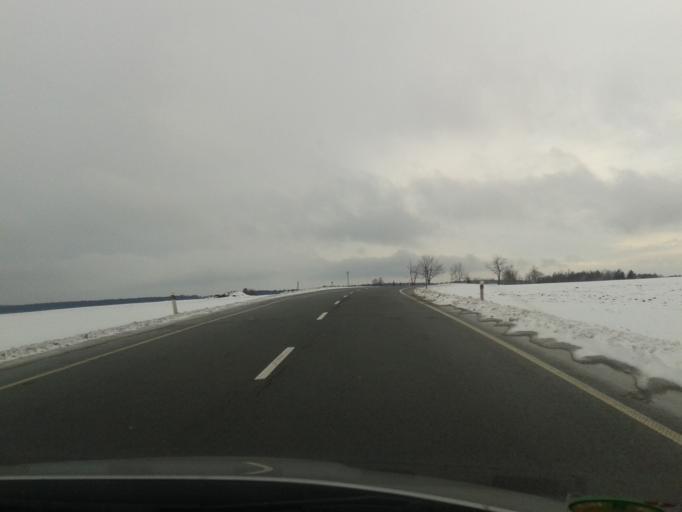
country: CZ
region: Olomoucky
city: Protivanov
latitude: 49.4698
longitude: 16.7752
